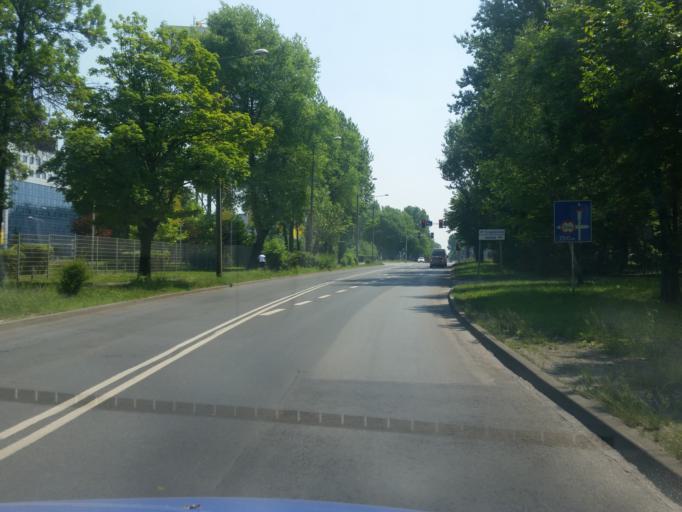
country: PL
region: Silesian Voivodeship
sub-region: Sosnowiec
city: Sosnowiec
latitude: 50.2552
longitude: 19.0910
